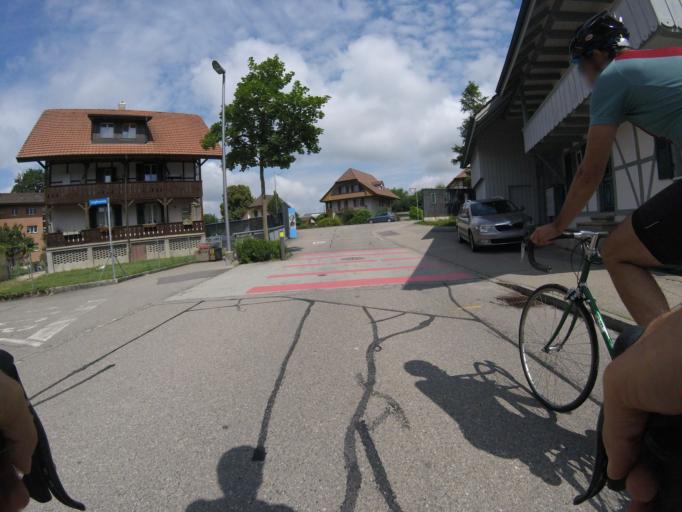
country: CH
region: Bern
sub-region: Bern-Mittelland District
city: Urtenen
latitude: 47.0184
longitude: 7.5064
